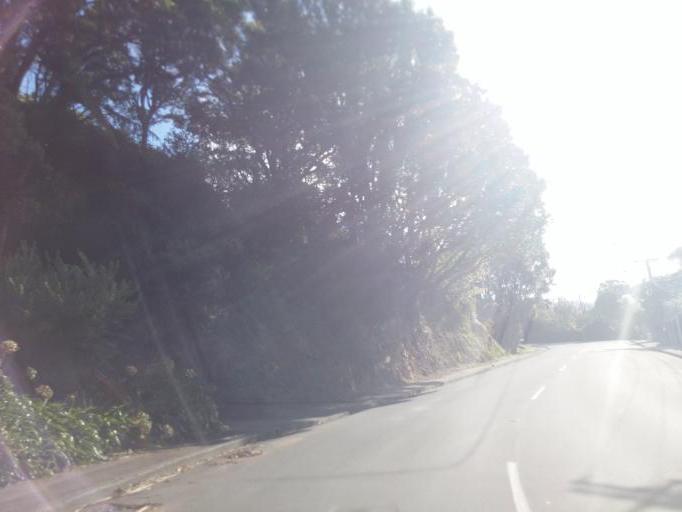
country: NZ
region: Wellington
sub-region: Wellington City
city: Kelburn
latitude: -41.2844
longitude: 174.7510
